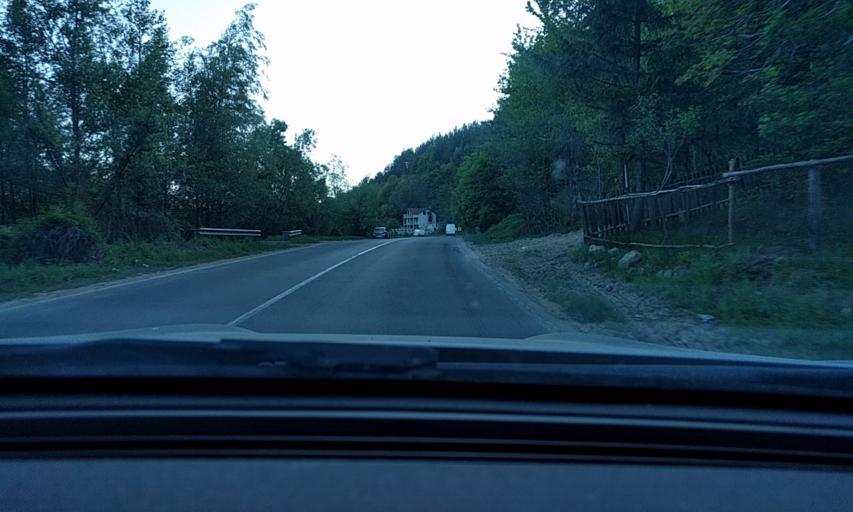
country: RO
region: Bacau
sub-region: Oras Slanic-Moldova
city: Slanic-Moldova
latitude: 46.1749
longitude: 26.4788
